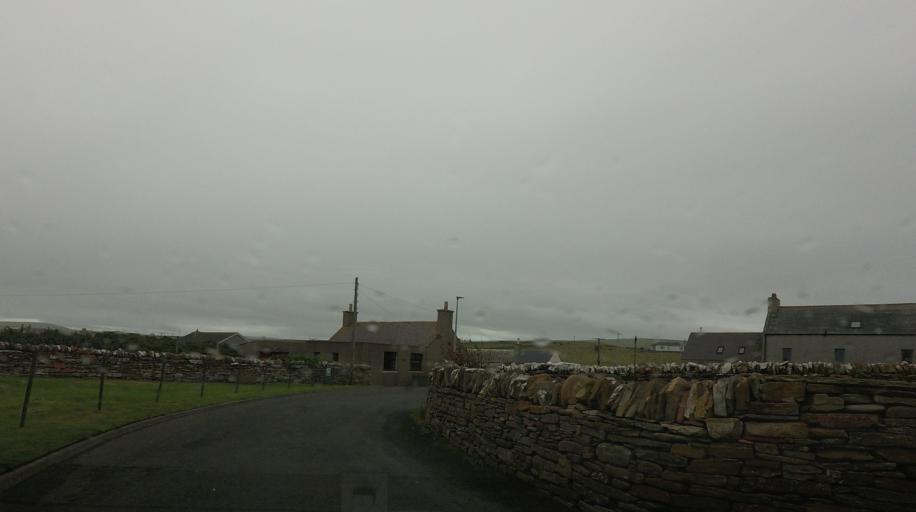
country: GB
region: Scotland
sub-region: Orkney Islands
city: Stromness
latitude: 59.1297
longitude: -3.3157
